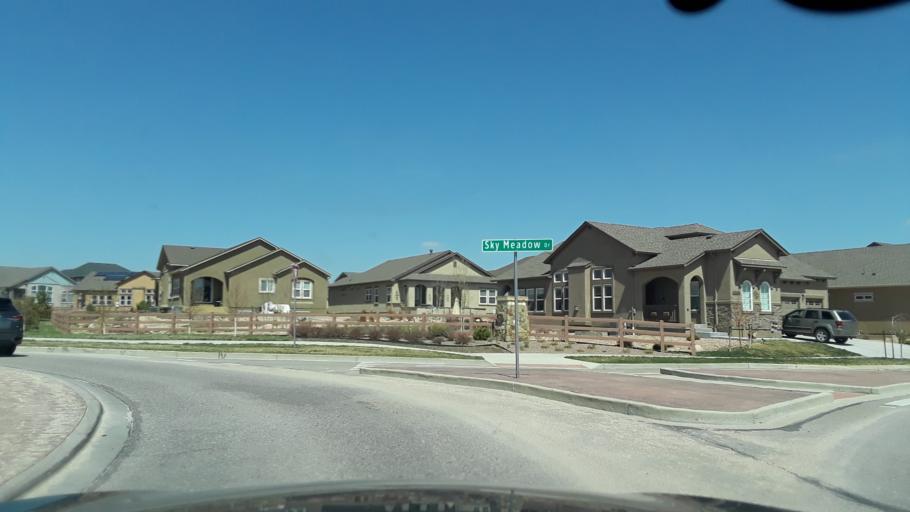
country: US
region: Colorado
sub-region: El Paso County
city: Black Forest
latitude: 38.9602
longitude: -104.7262
